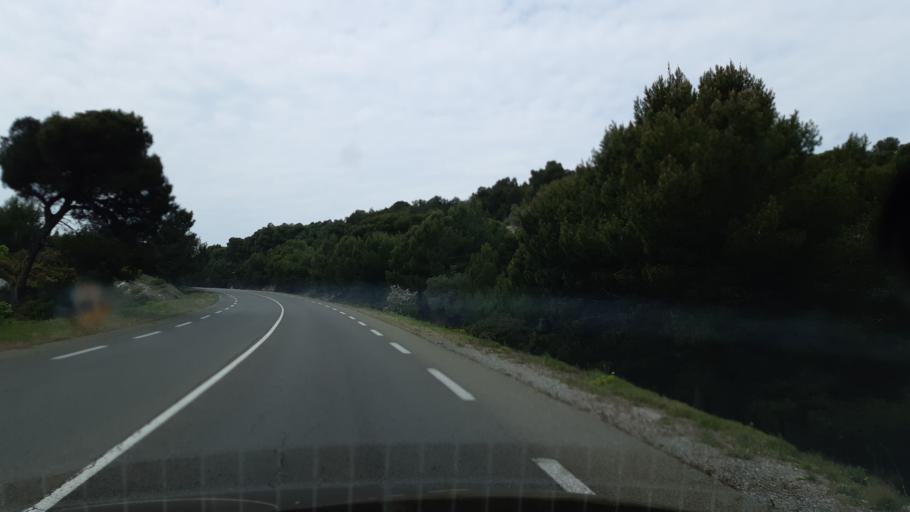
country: FR
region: Languedoc-Roussillon
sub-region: Departement de l'Aude
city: Gruissan
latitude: 43.1207
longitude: 3.0819
